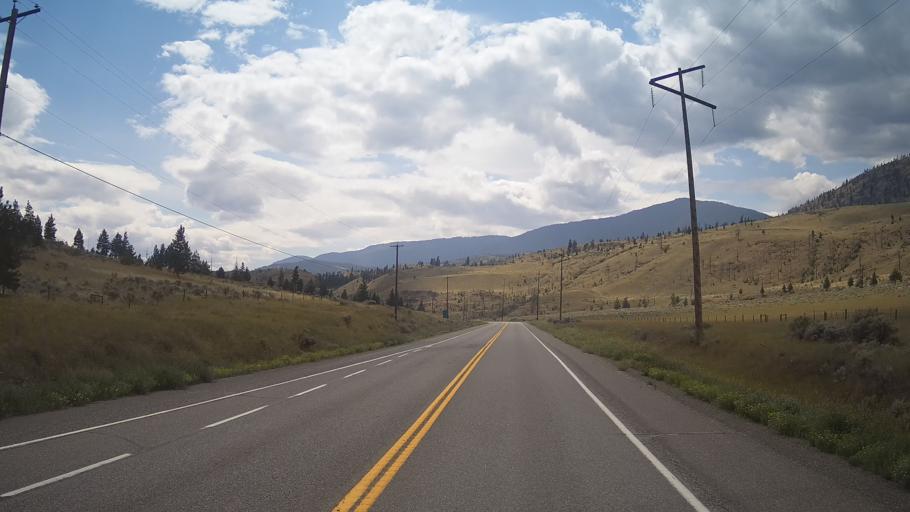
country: CA
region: British Columbia
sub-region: Thompson-Nicola Regional District
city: Ashcroft
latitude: 50.6363
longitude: -121.3451
